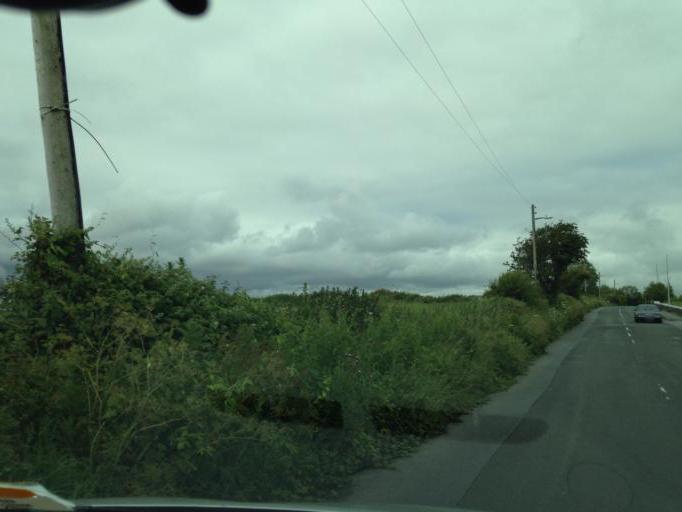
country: IE
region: Connaught
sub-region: County Galway
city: Gaillimh
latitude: 53.2851
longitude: -9.0573
